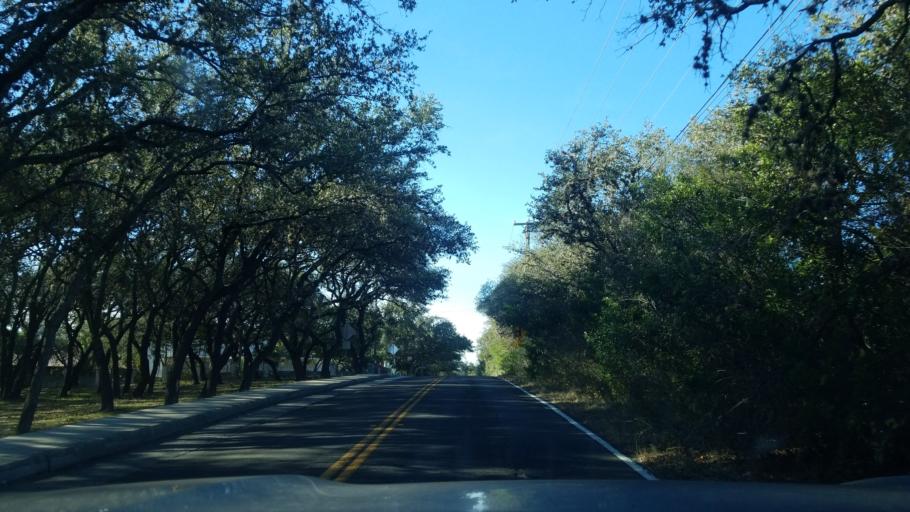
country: US
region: Texas
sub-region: Bexar County
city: Balcones Heights
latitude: 29.5323
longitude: -98.5687
